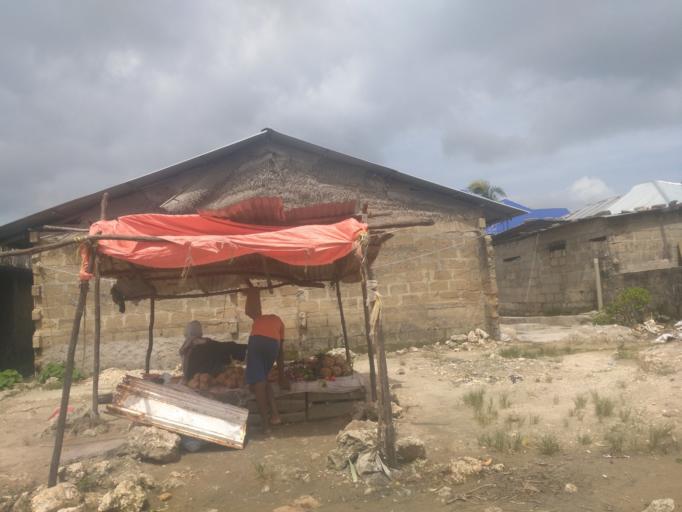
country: TZ
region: Zanzibar Urban/West
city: Zanzibar
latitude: -6.1759
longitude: 39.2401
